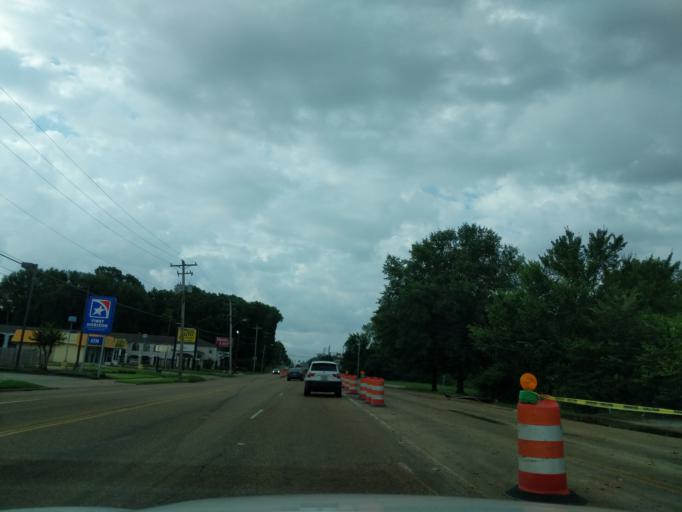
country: US
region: Tennessee
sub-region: Shelby County
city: New South Memphis
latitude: 35.0536
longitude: -90.0250
